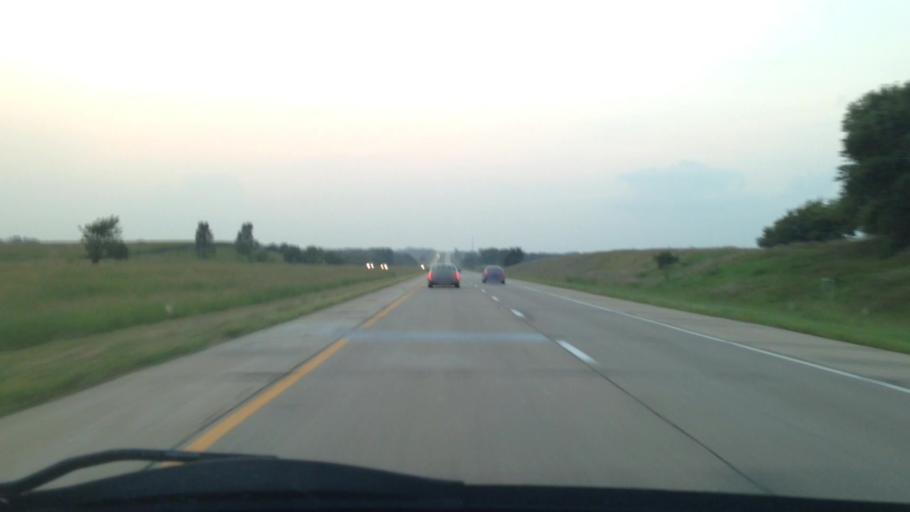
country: US
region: Iowa
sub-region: Benton County
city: Urbana
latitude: 42.2891
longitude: -91.9495
